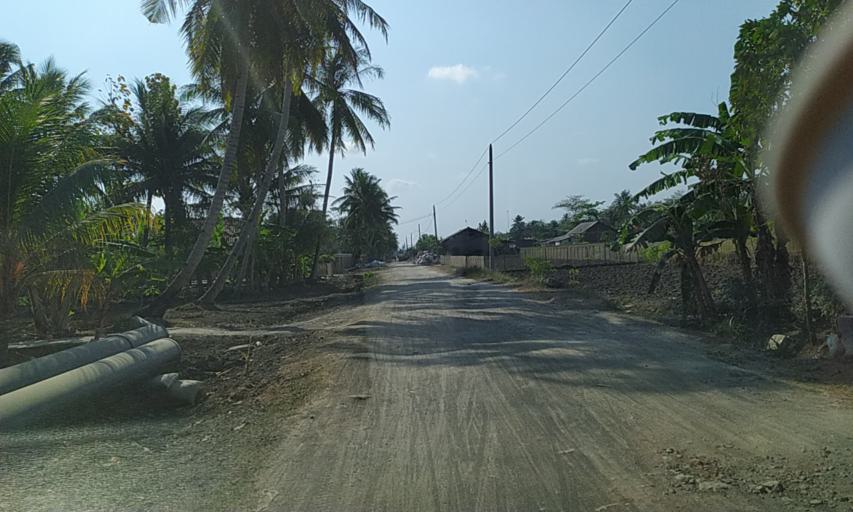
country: ID
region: Central Java
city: Alurbulu
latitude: -7.5074
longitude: 108.8362
